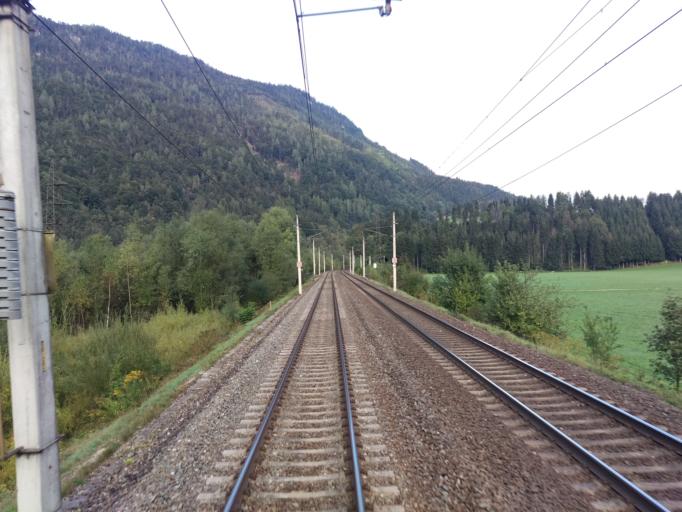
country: AT
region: Salzburg
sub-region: Politischer Bezirk Sankt Johann im Pongau
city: Bischofshofen
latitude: 47.4315
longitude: 13.2172
